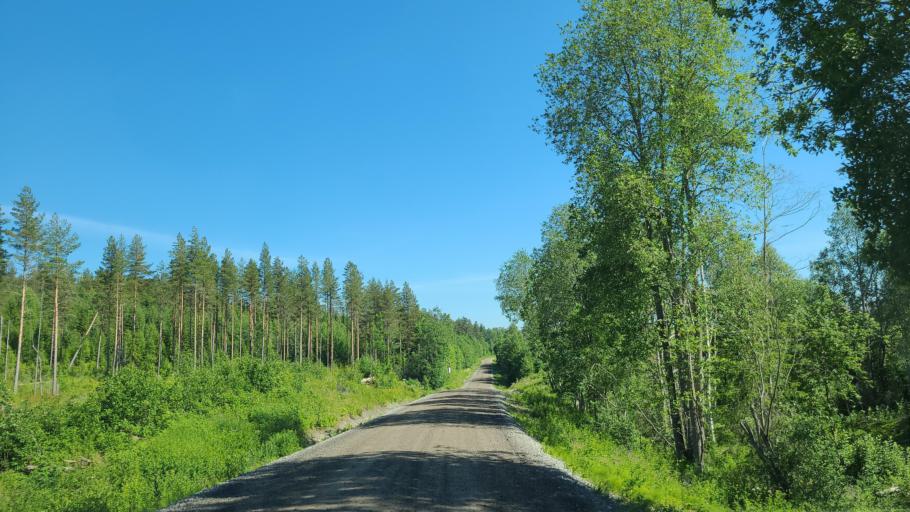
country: SE
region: Vaesterbotten
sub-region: Bjurholms Kommun
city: Bjurholm
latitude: 63.6797
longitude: 18.9945
